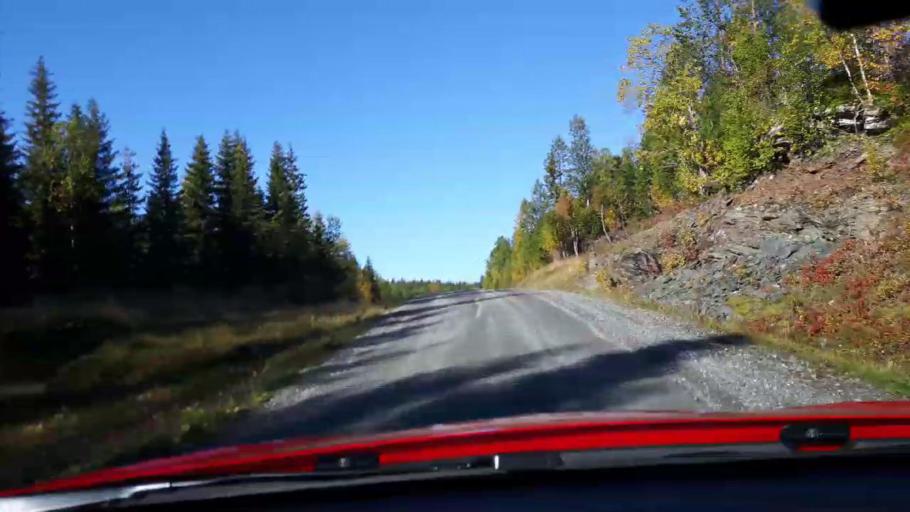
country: NO
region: Nord-Trondelag
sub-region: Lierne
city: Sandvika
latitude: 64.6083
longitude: 13.7082
